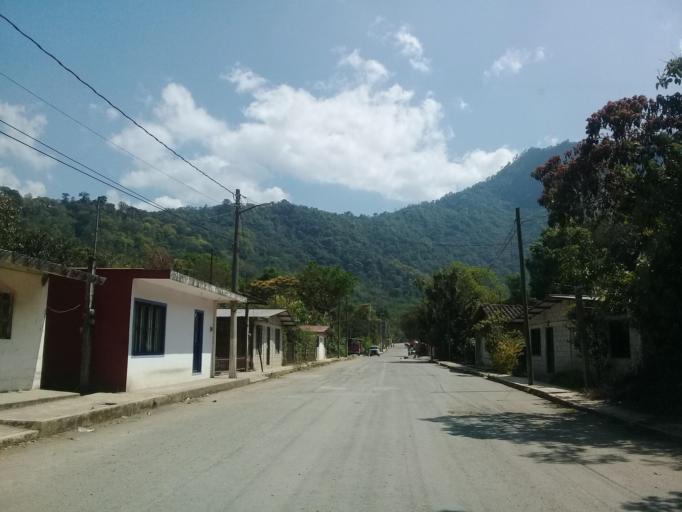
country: MX
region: Veracruz
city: Jalapilla
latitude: 18.8085
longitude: -97.0708
